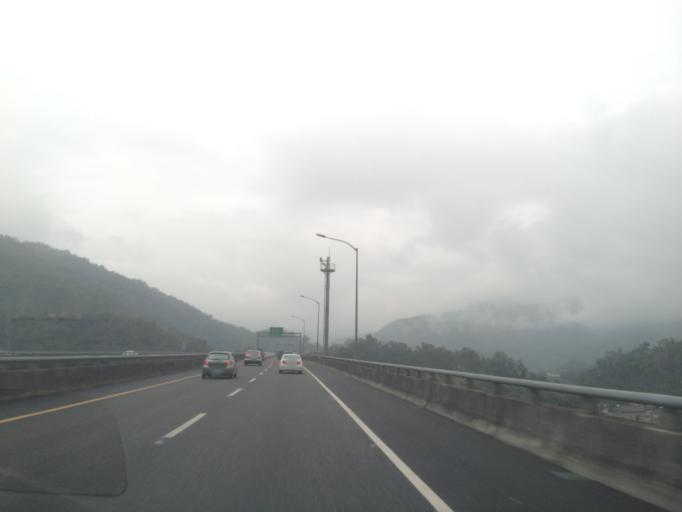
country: TW
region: Taiwan
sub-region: Nantou
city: Puli
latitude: 23.9792
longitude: 120.9021
